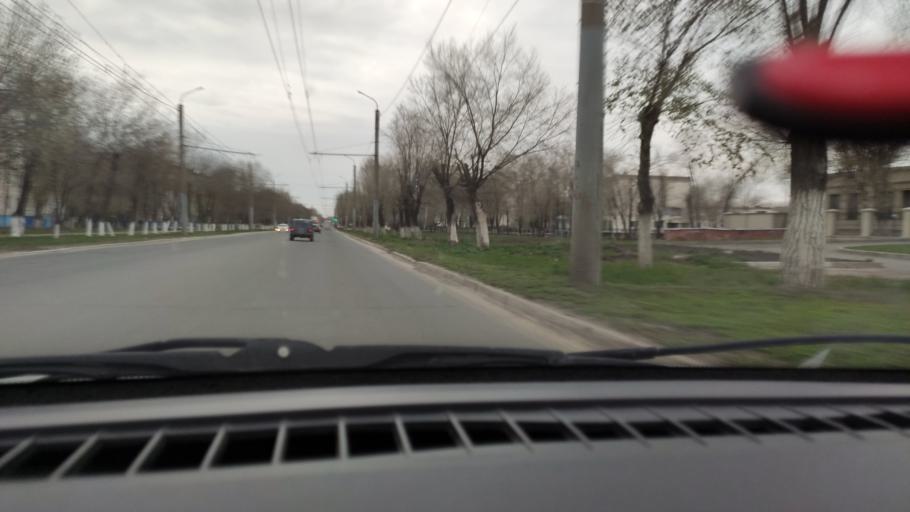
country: RU
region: Orenburg
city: Orenburg
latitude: 51.8432
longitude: 55.1302
